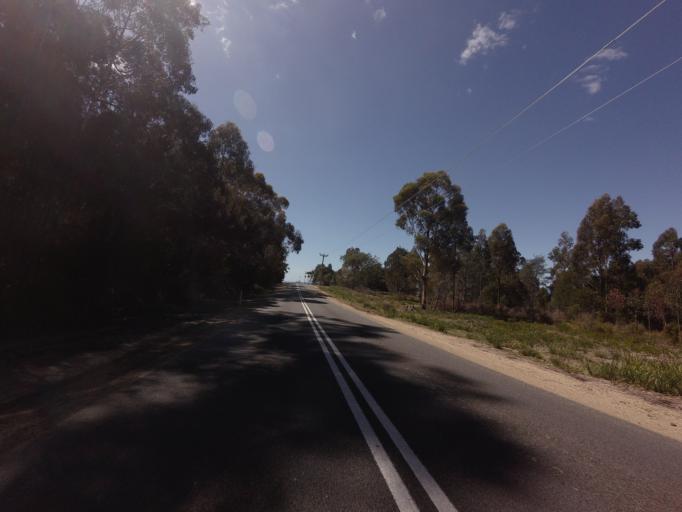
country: AU
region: Tasmania
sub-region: Break O'Day
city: St Helens
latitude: -41.6710
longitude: 148.2815
